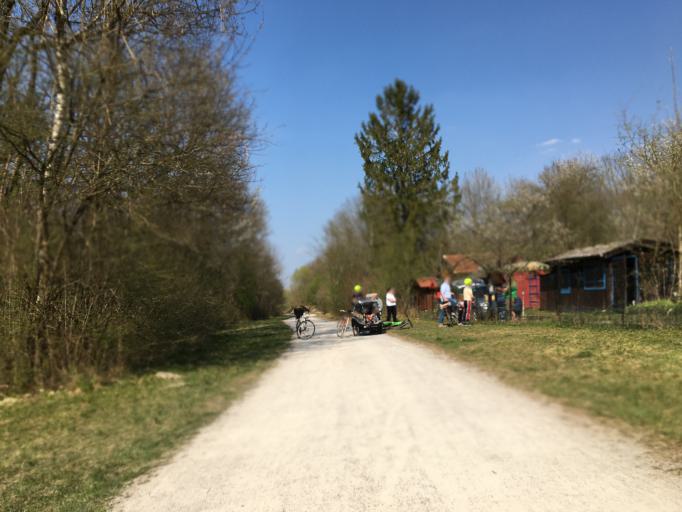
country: DE
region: Bavaria
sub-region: Upper Bavaria
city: Unterfoehring
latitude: 48.1802
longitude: 11.6247
